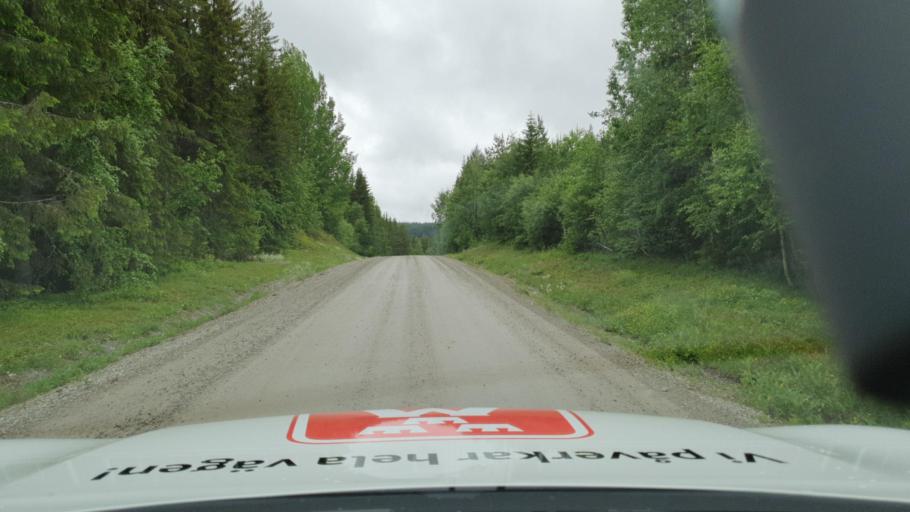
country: SE
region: Vaesterbotten
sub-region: Dorotea Kommun
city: Dorotea
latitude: 64.0295
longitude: 16.7789
